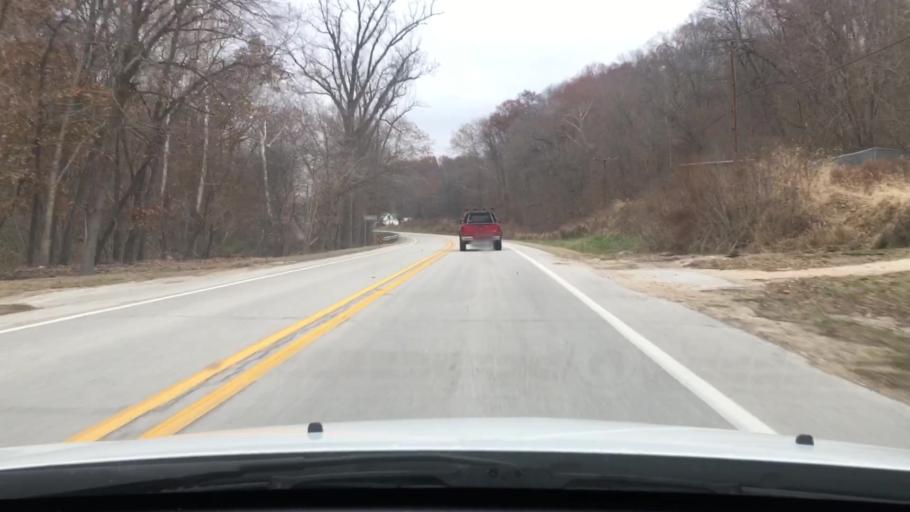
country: US
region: Missouri
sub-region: Pike County
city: Louisiana
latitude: 39.5154
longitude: -90.9622
